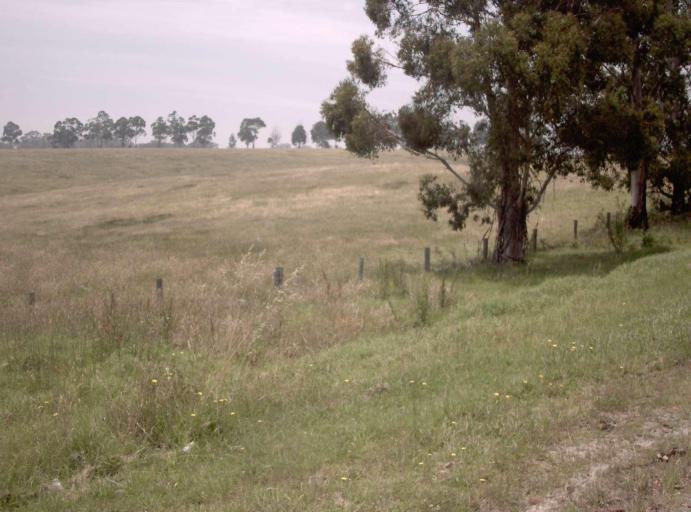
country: AU
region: Victoria
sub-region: Latrobe
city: Traralgon
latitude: -38.2480
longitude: 146.6519
